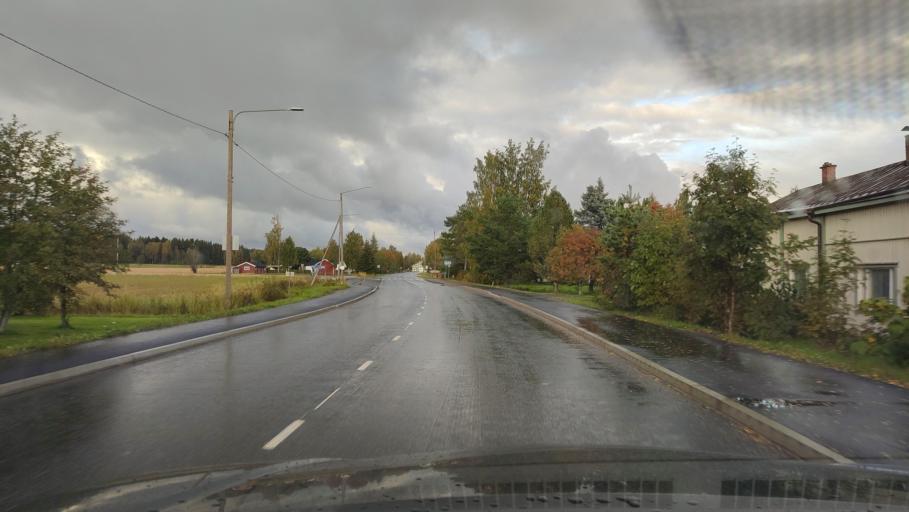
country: FI
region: Southern Ostrobothnia
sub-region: Suupohja
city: Karijoki
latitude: 62.3086
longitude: 21.7090
